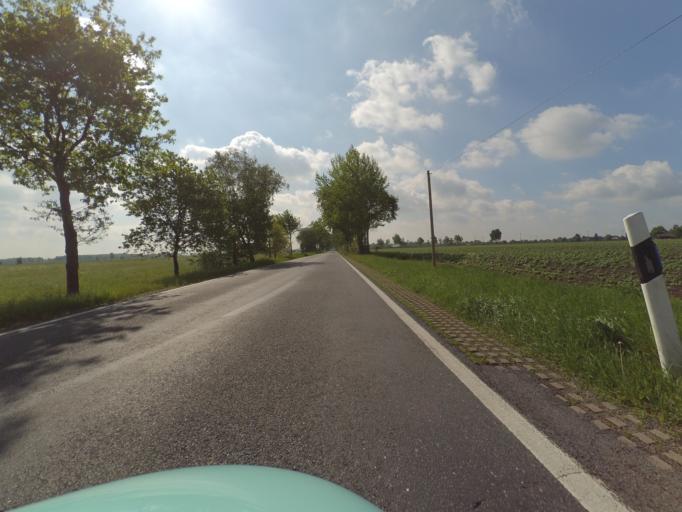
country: DE
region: Lower Saxony
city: Arpke
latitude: 52.4218
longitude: 10.1300
